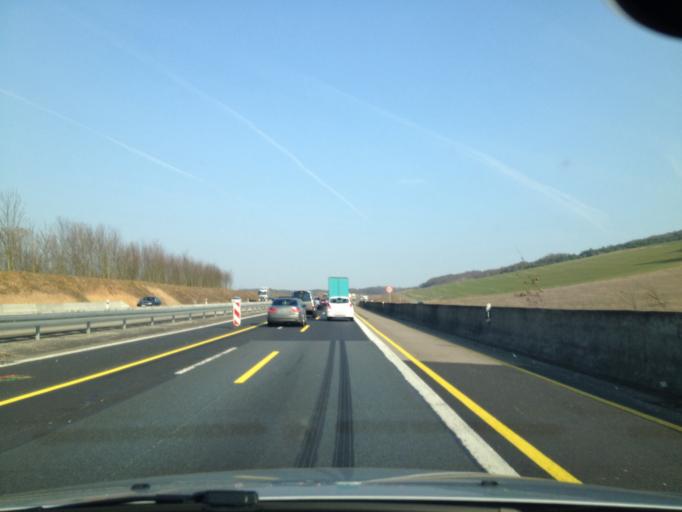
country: DE
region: Bavaria
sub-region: Regierungsbezirk Unterfranken
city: Neubrunn
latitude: 49.7639
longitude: 9.6130
